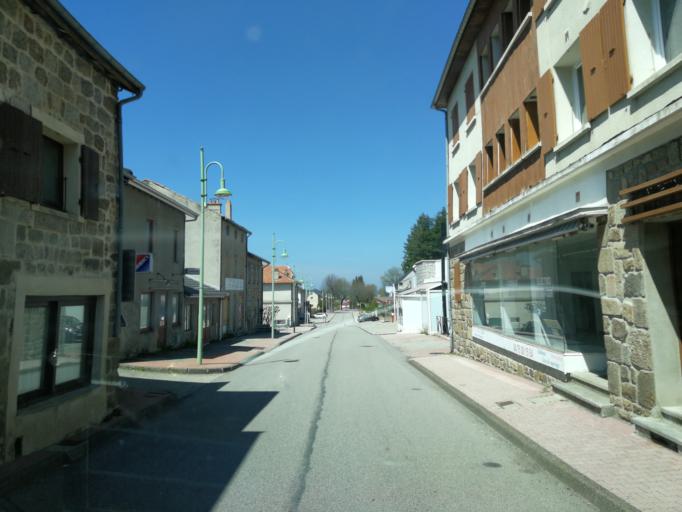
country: FR
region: Rhone-Alpes
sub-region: Departement de l'Ardeche
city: Saint-Agreve
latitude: 45.0104
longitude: 4.3945
